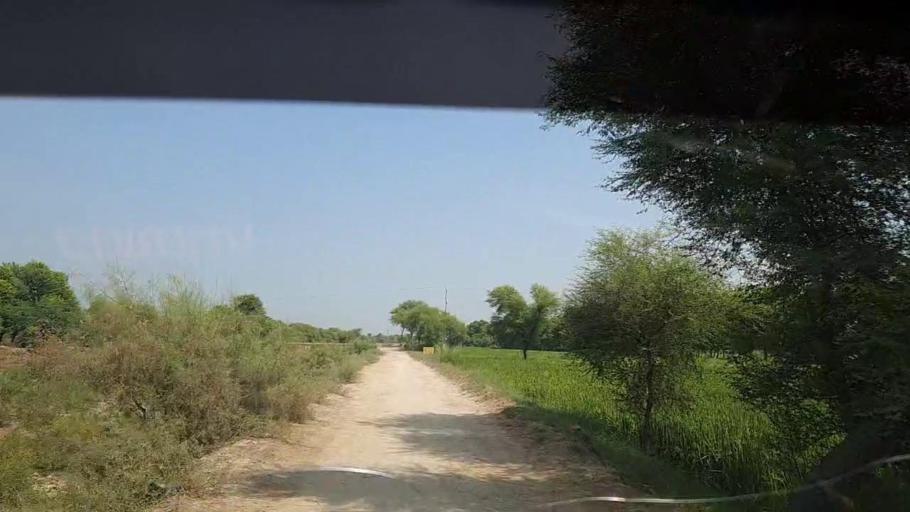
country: PK
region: Sindh
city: Tangwani
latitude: 28.2311
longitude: 68.9371
